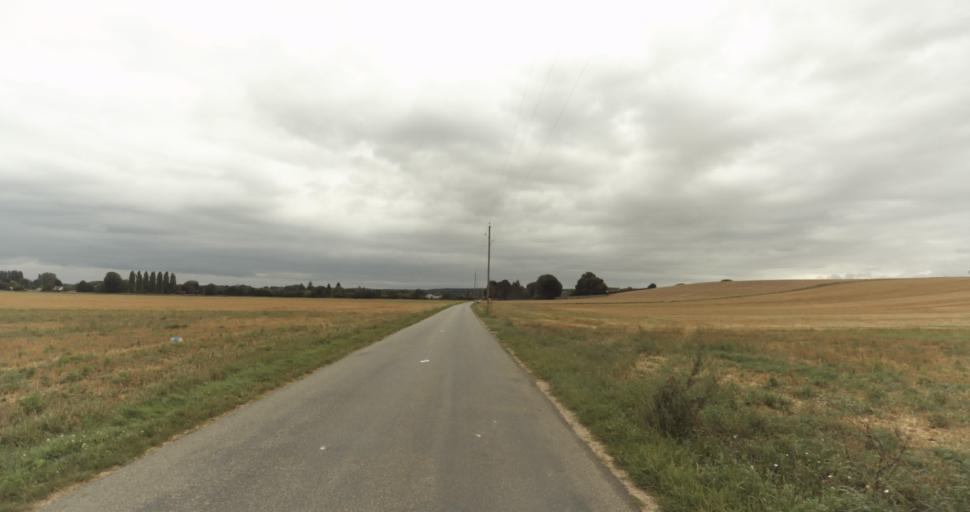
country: FR
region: Haute-Normandie
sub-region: Departement de l'Eure
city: Houlbec-Cocherel
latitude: 49.0581
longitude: 1.2983
